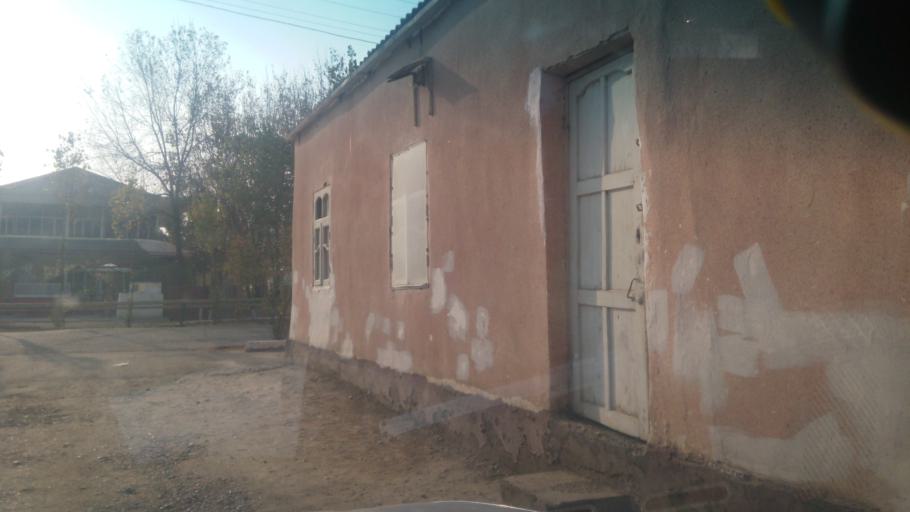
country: UZ
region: Sirdaryo
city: Guliston
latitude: 40.5189
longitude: 68.7759
